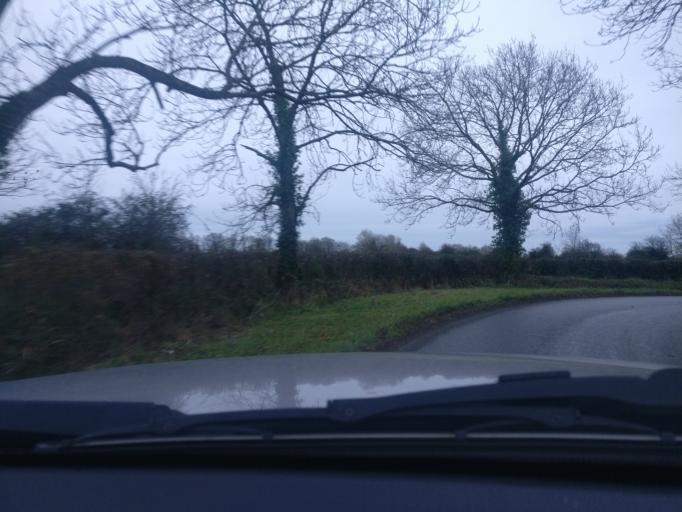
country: IE
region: Leinster
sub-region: Kildare
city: Maynooth
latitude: 53.4160
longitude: -6.6097
